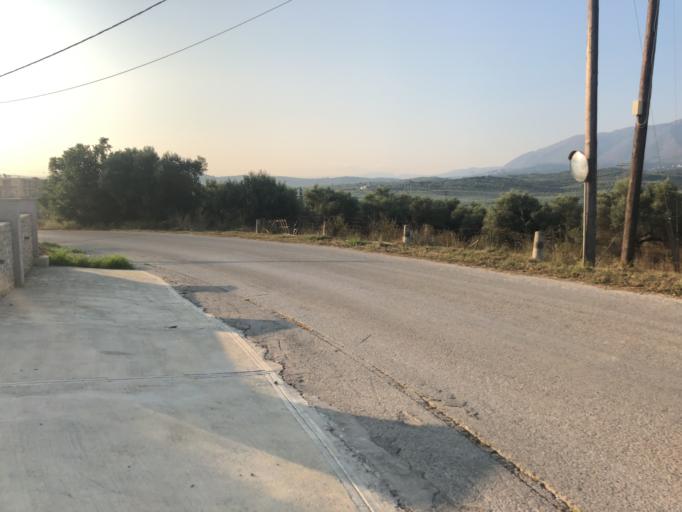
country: GR
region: Crete
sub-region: Nomos Chanias
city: Georgioupolis
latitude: 35.3479
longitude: 24.2859
